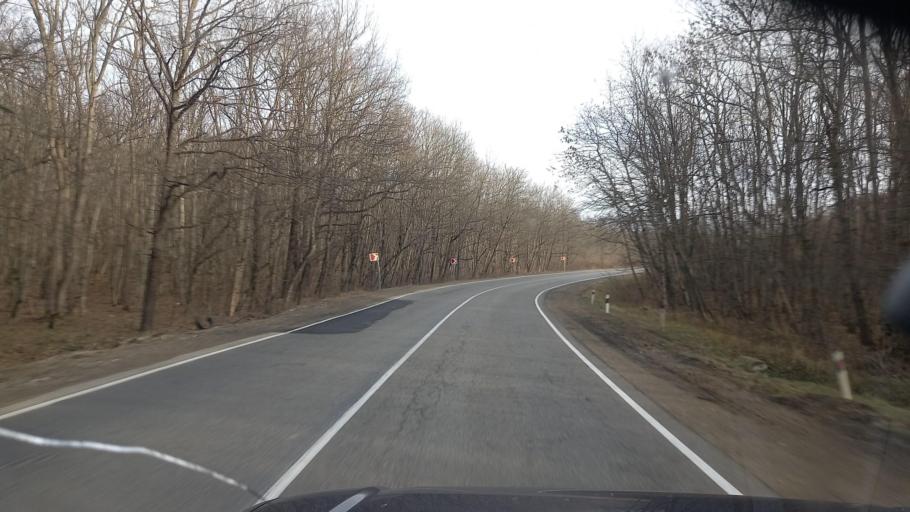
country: RU
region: Krasnodarskiy
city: Khadyzhensk
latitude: 44.6552
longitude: 39.4823
